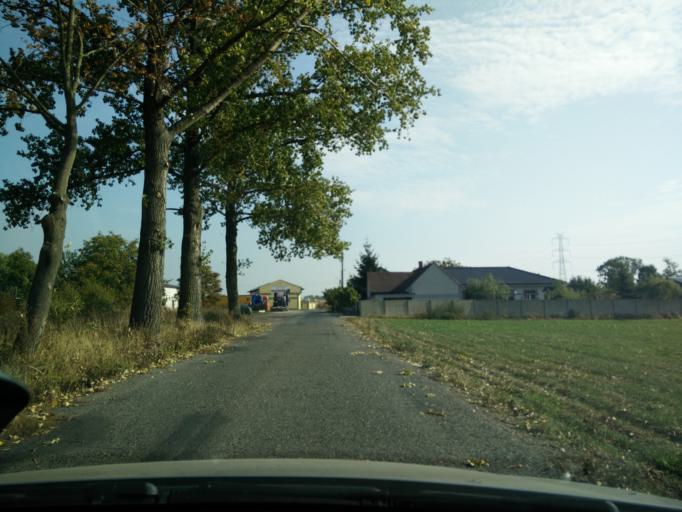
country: PL
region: Greater Poland Voivodeship
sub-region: Powiat sredzki
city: Sroda Wielkopolska
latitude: 52.3015
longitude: 17.2719
